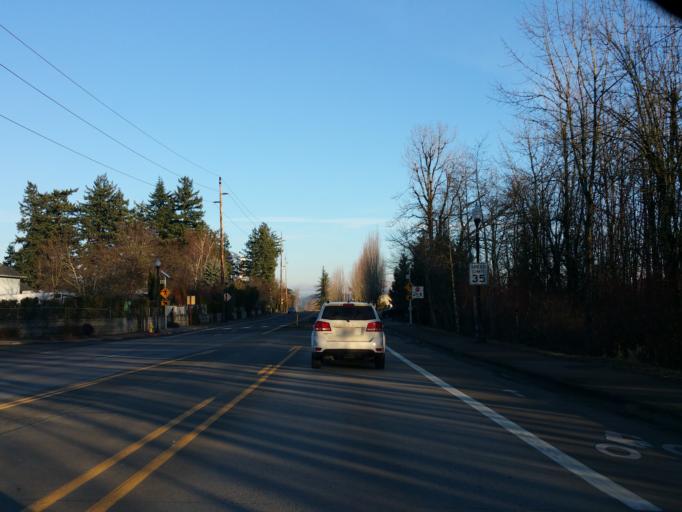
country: US
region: Oregon
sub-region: Multnomah County
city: Fairview
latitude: 45.5337
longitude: -122.4454
